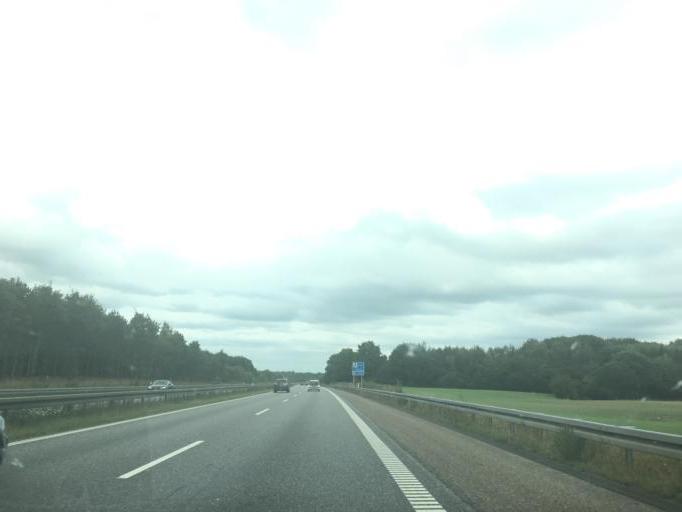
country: DK
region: Zealand
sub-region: Soro Kommune
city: Soro
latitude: 55.4453
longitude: 11.5184
